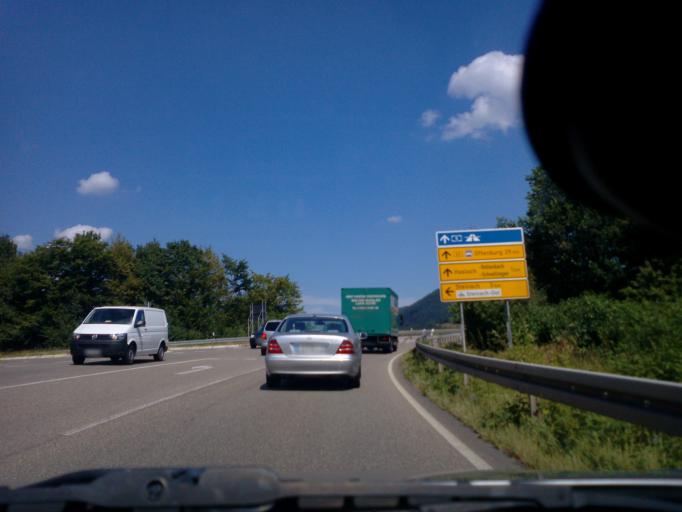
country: DE
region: Baden-Wuerttemberg
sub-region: Freiburg Region
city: Steinach
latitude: 48.2837
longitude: 8.0744
